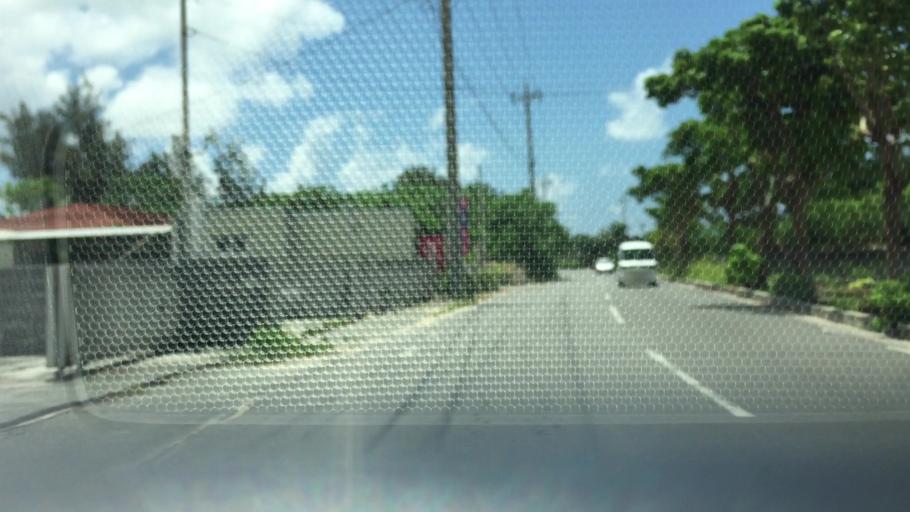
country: JP
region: Okinawa
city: Ishigaki
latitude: 24.3616
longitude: 124.1182
